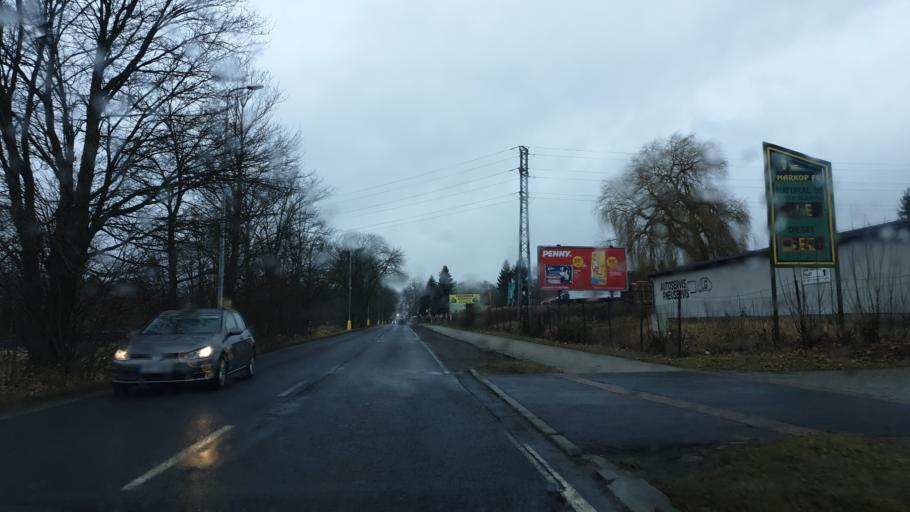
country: CZ
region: Karlovarsky
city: As
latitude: 50.2049
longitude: 12.2080
